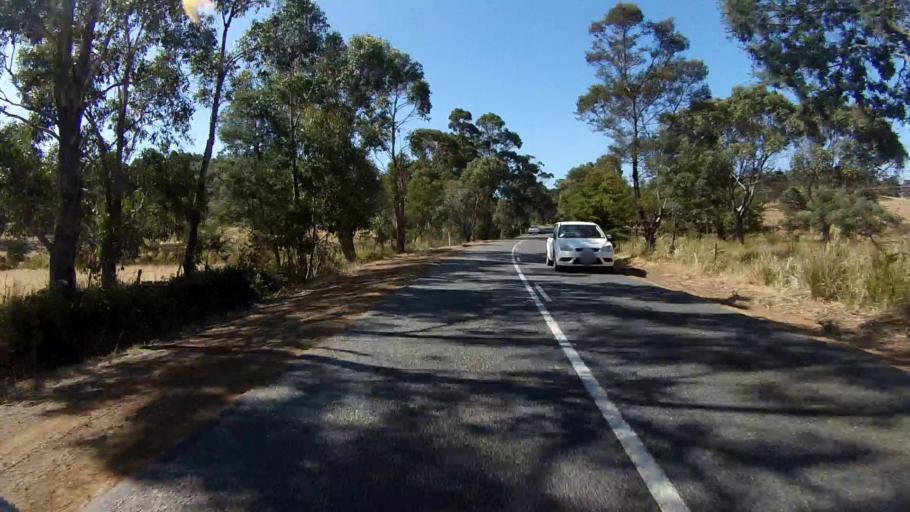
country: AU
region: Tasmania
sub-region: Sorell
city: Sorell
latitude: -42.3179
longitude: 147.9575
